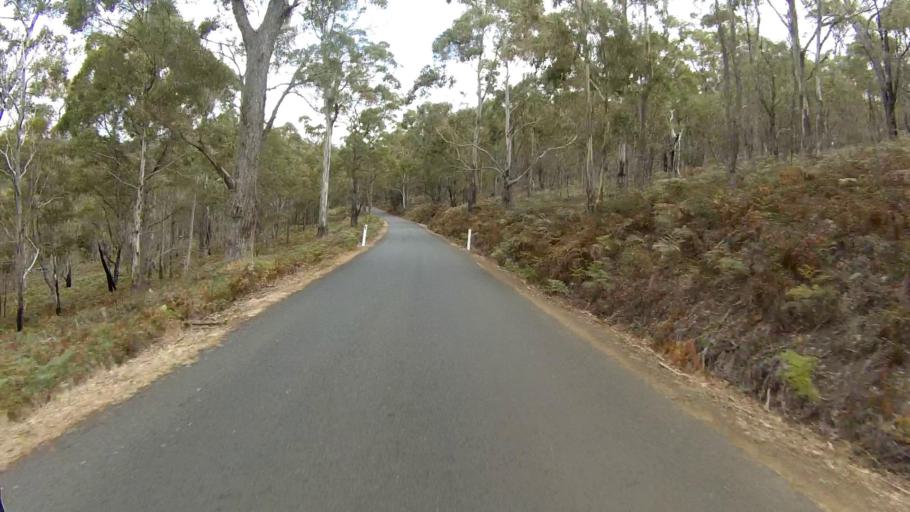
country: AU
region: Tasmania
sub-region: Sorell
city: Sorell
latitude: -42.6016
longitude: 147.9242
